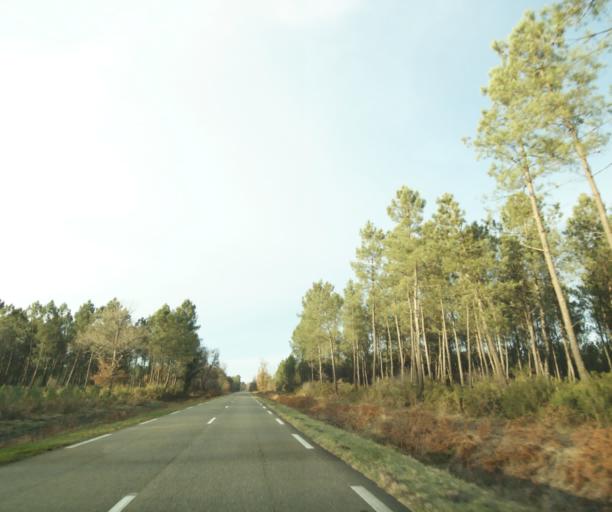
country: FR
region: Aquitaine
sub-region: Departement des Landes
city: Gabarret
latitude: 44.0464
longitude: -0.0395
